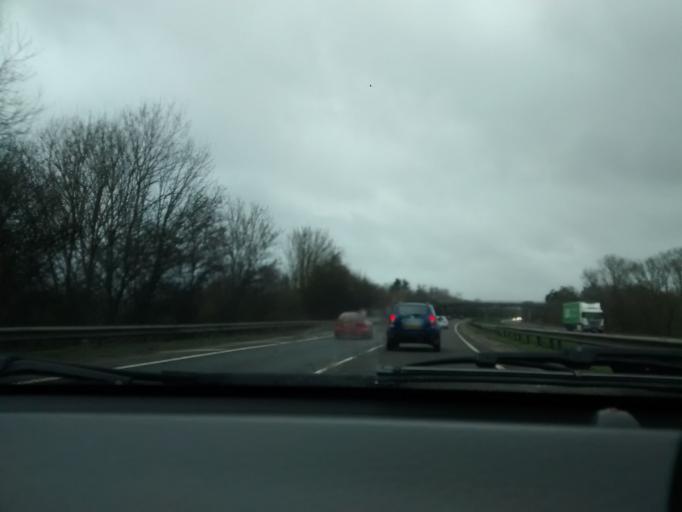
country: GB
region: England
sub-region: Suffolk
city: Bramford
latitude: 52.1153
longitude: 1.1034
